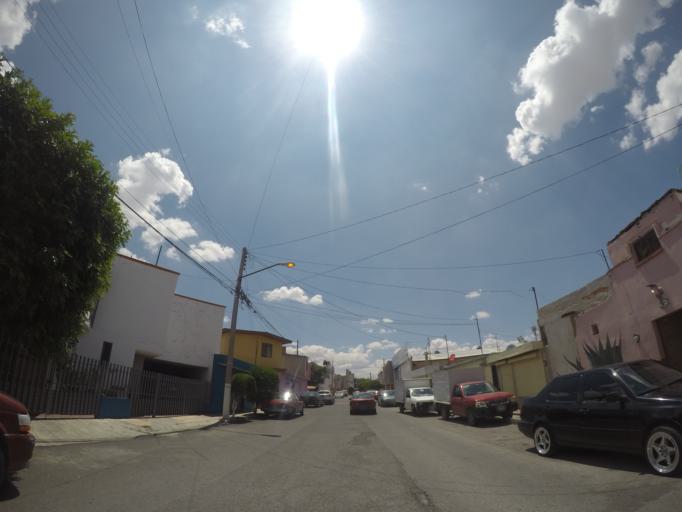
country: MX
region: San Luis Potosi
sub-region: San Luis Potosi
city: San Luis Potosi
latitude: 22.1438
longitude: -100.9916
